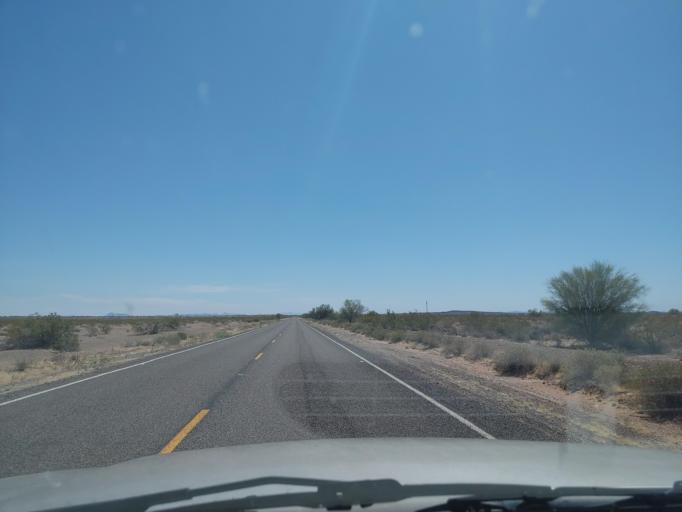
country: US
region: Arizona
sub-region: Maricopa County
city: Gila Bend
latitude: 32.8810
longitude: -113.2268
